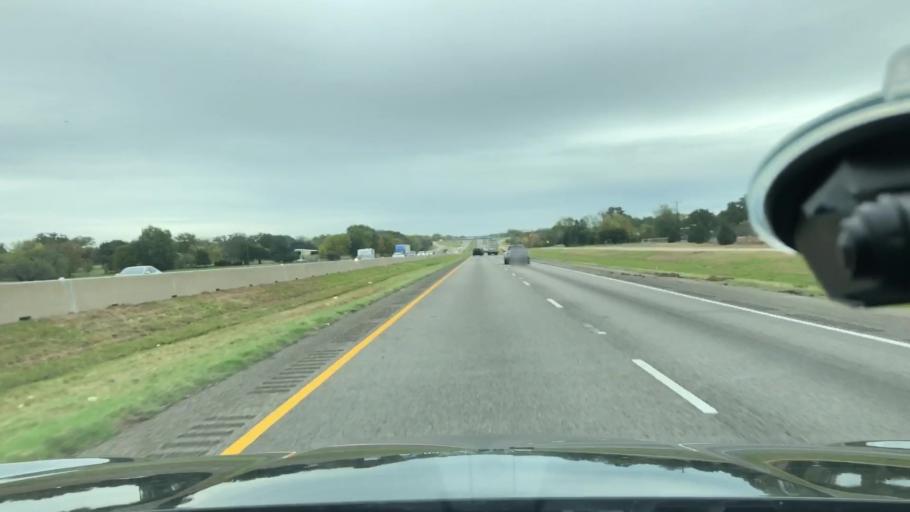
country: US
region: Texas
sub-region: Hopkins County
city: Sulphur Springs
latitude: 33.1467
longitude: -95.5085
